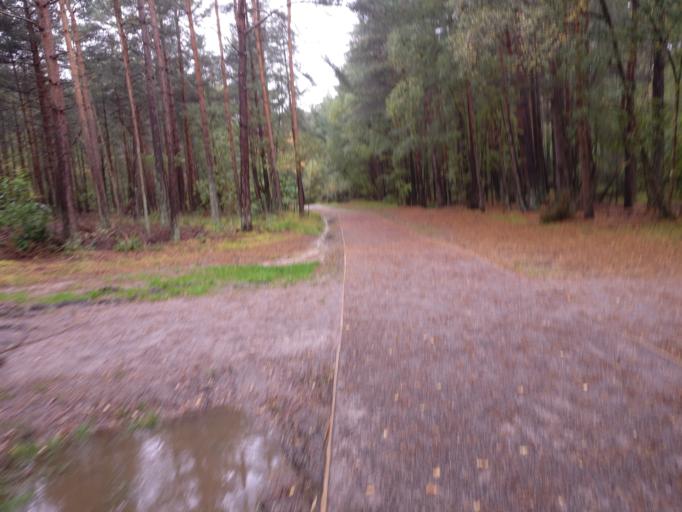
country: GB
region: England
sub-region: Surrey
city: Frimley
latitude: 51.3183
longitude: -0.7175
